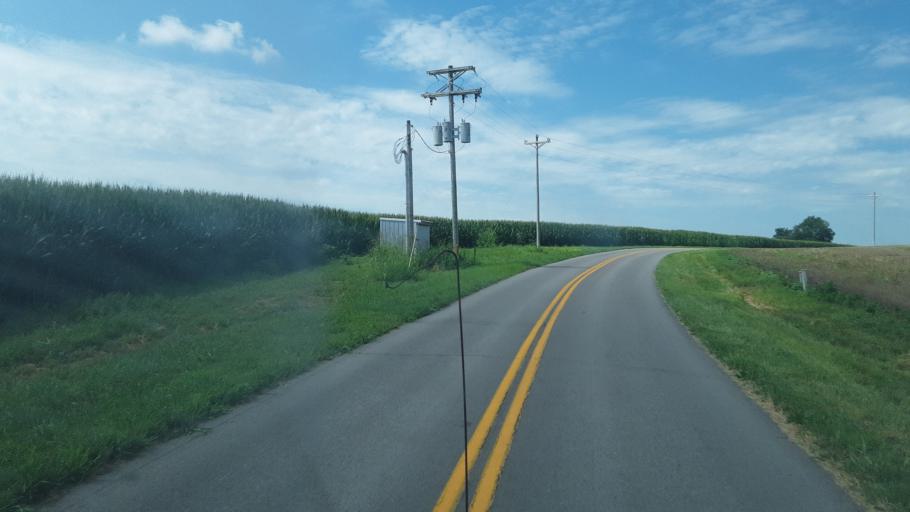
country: US
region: Kentucky
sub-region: Christian County
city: Oak Grove
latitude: 36.7437
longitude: -87.3173
